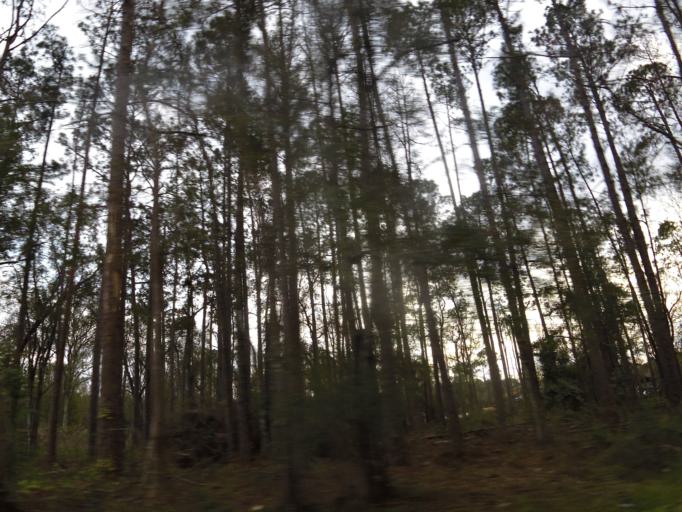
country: US
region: Florida
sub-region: Duval County
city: Baldwin
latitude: 30.2961
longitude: -81.9789
